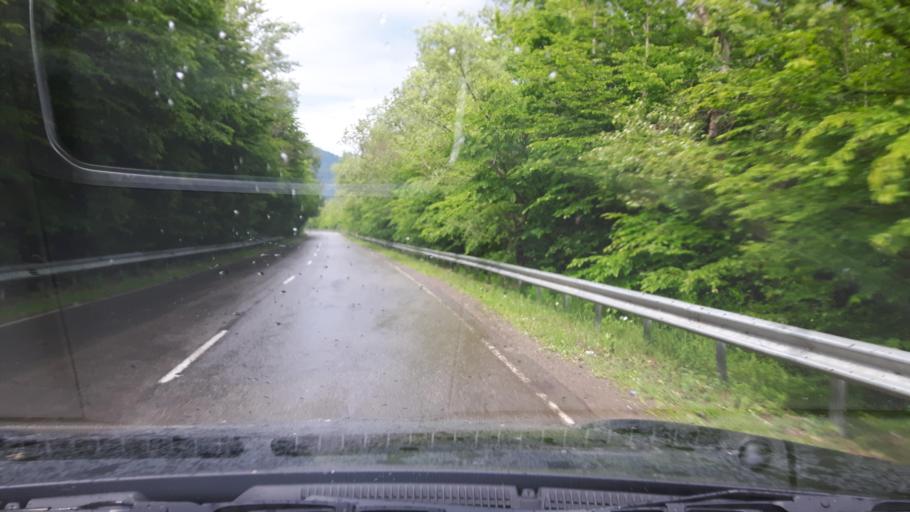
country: GE
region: Kakheti
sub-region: Telavi
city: Telavi
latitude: 41.8651
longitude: 45.3523
